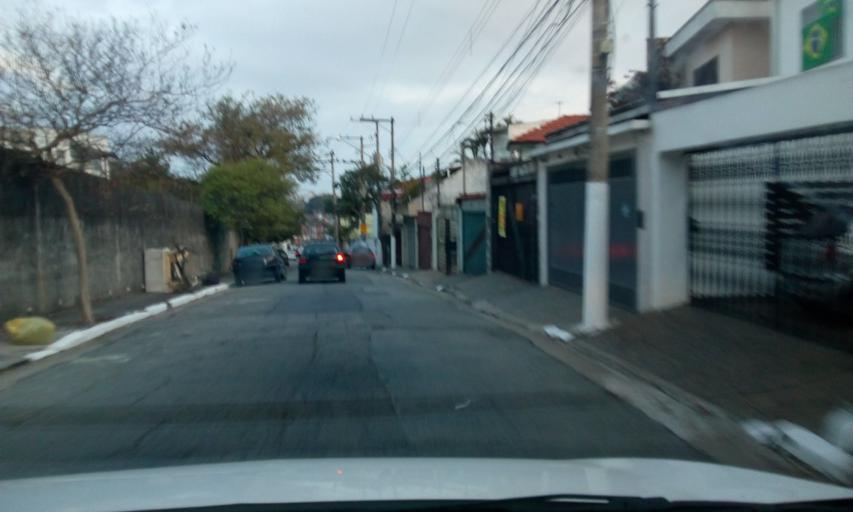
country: BR
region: Sao Paulo
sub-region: Diadema
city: Diadema
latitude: -23.6333
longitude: -46.6466
